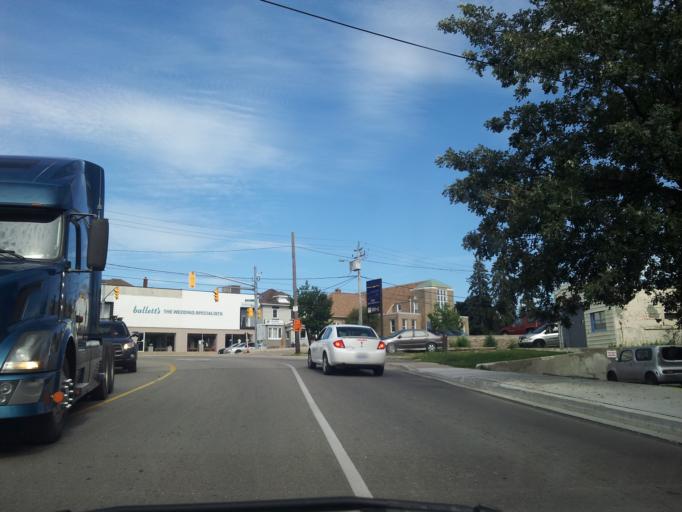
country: CA
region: Ontario
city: Kitchener
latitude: 43.4439
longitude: -80.4775
